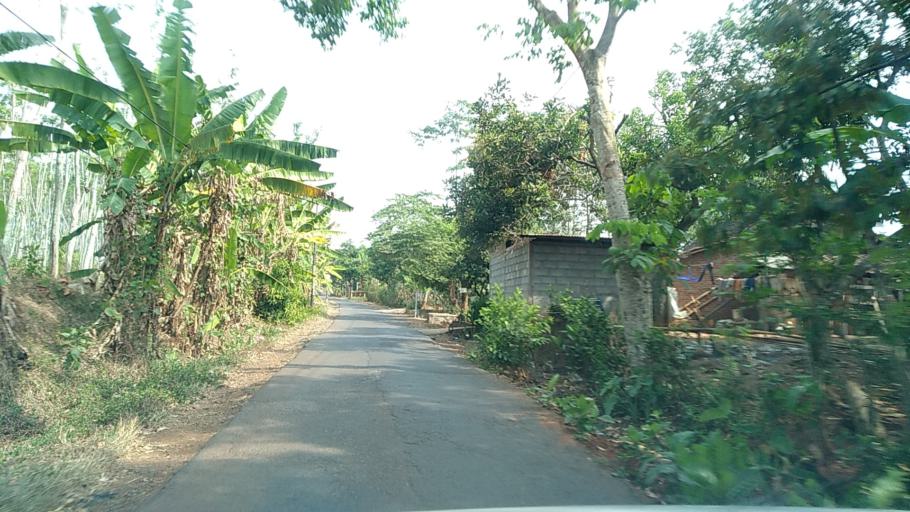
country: ID
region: Central Java
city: Semarang
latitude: -7.0247
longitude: 110.3115
